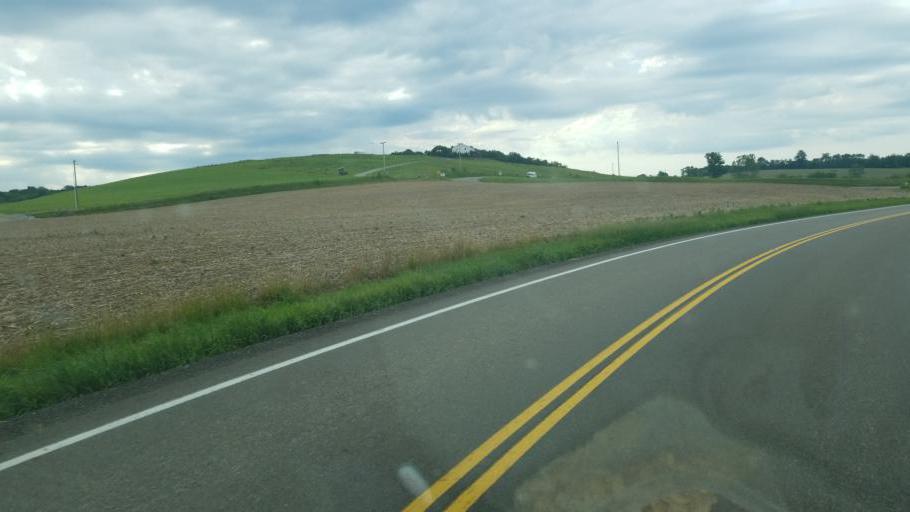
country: US
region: Ohio
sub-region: Knox County
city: Danville
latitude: 40.4740
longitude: -82.2750
